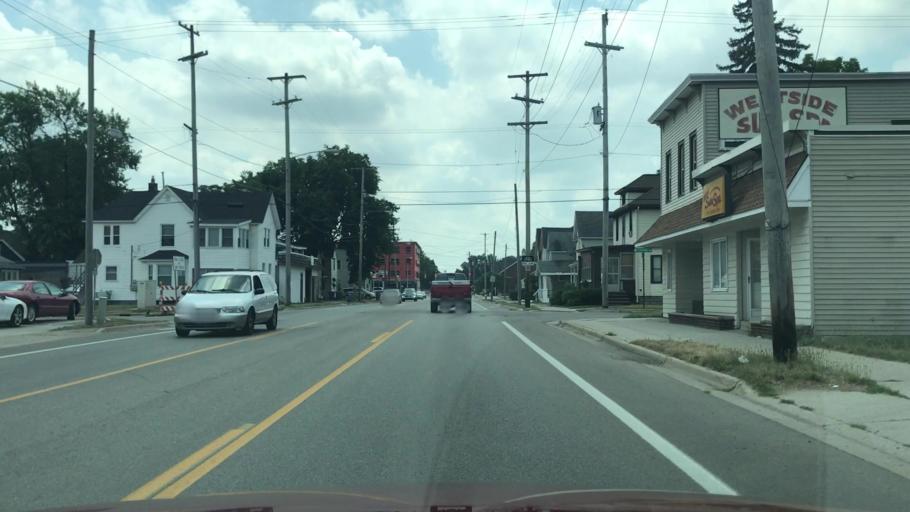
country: US
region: Michigan
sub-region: Kent County
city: Grand Rapids
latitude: 42.9874
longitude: -85.6882
